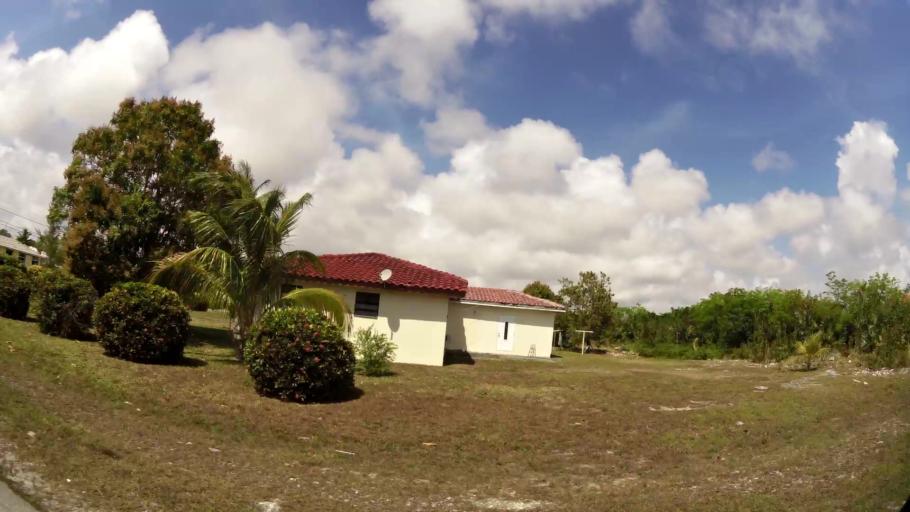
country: BS
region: Freeport
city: Freeport
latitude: 26.5055
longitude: -78.7180
